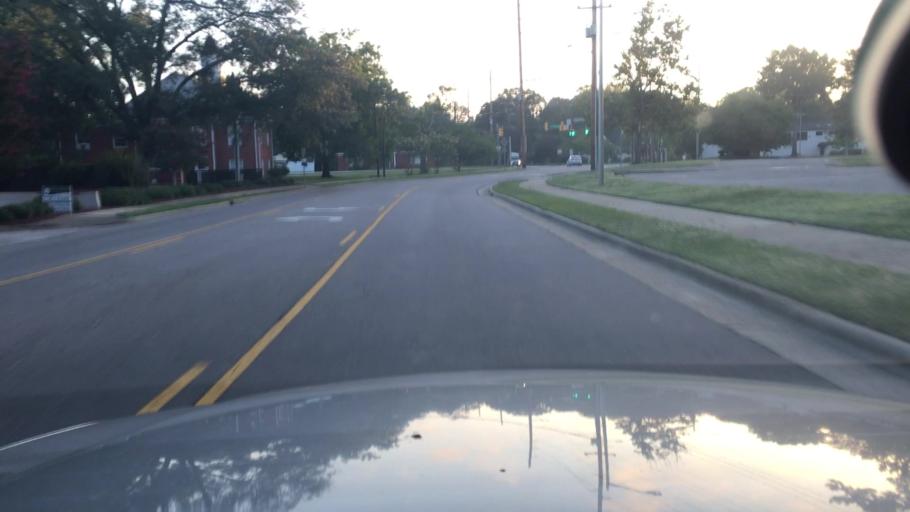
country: US
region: North Carolina
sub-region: Cumberland County
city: Fayetteville
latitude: 35.0688
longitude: -78.9227
